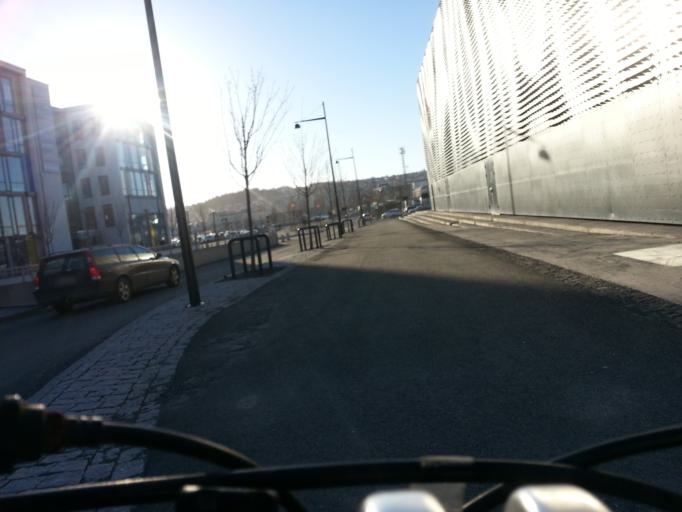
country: NO
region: Sor-Trondelag
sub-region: Trondheim
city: Trondheim
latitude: 63.4407
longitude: 10.4027
